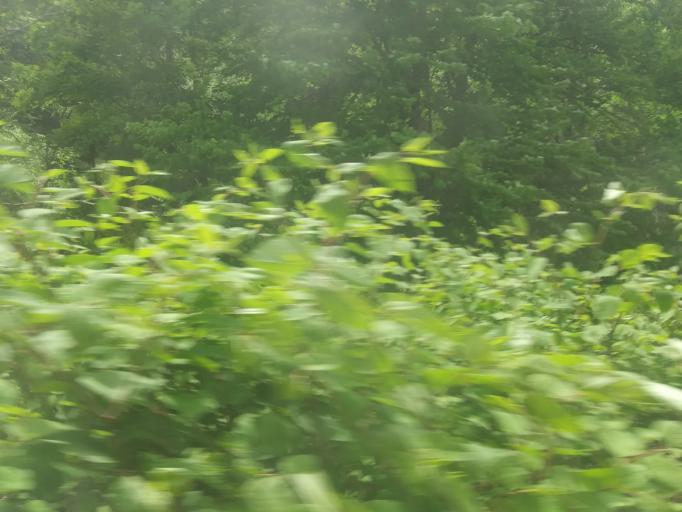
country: US
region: Massachusetts
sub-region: Franklin County
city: Buckland
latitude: 42.5694
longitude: -72.8105
